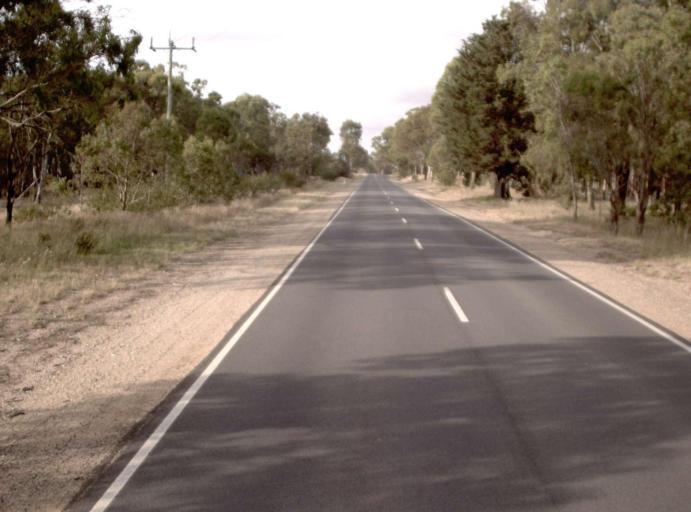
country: AU
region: Victoria
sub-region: Wellington
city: Sale
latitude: -37.9317
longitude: 146.9916
